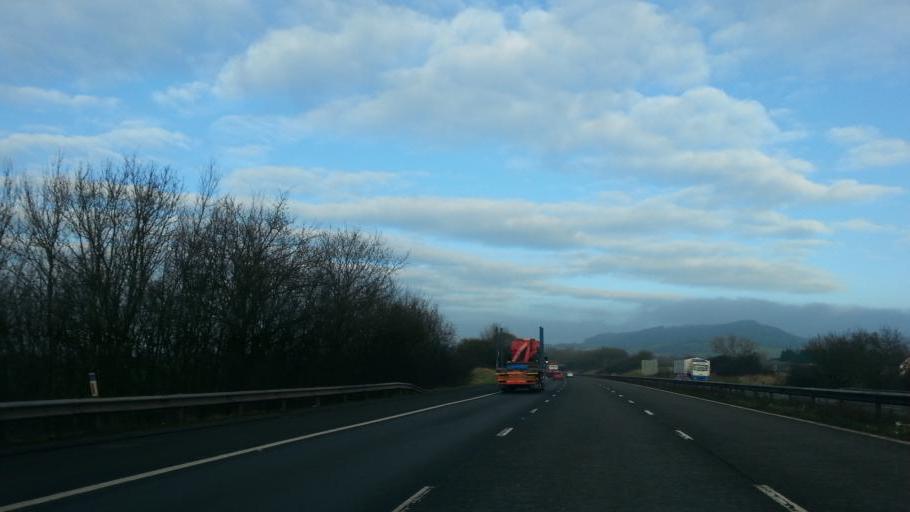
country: GB
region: England
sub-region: South Gloucestershire
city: Charfield
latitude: 51.6646
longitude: -2.4141
